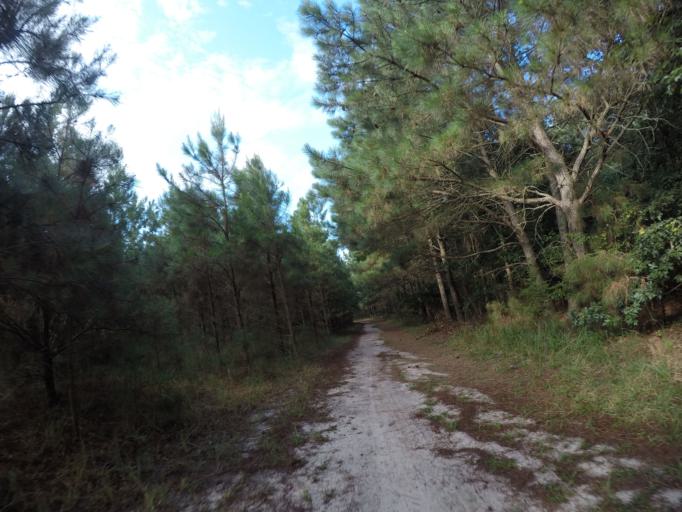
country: US
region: Delaware
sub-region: Sussex County
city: Ocean View
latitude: 38.5698
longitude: -75.0728
